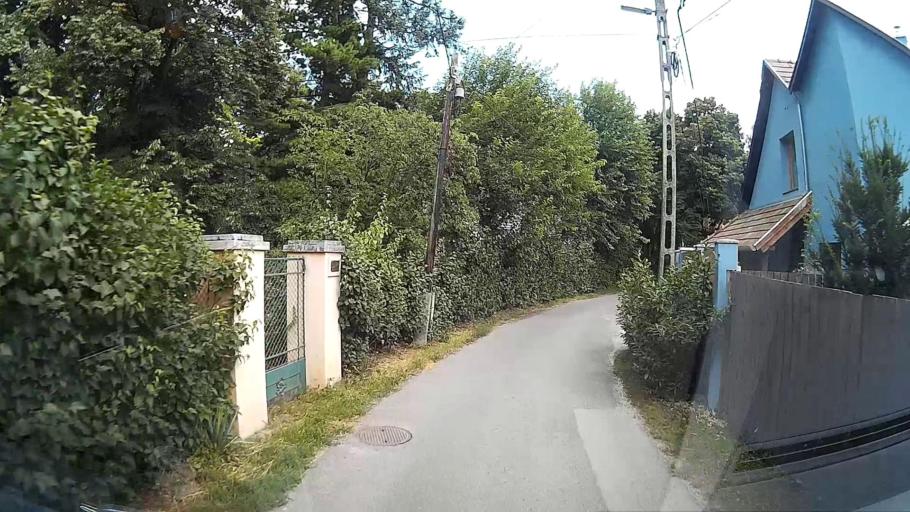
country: HU
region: Pest
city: Szentendre
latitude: 47.6736
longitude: 19.0618
